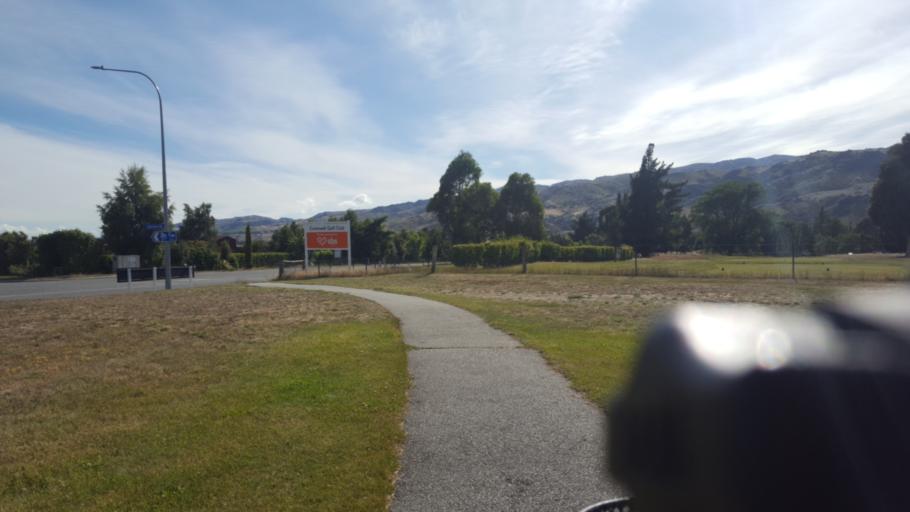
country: NZ
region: Otago
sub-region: Queenstown-Lakes District
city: Wanaka
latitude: -45.0347
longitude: 169.2020
